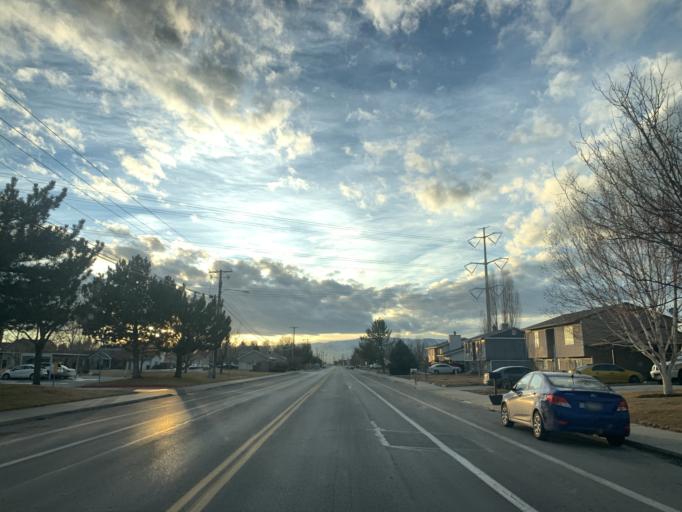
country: US
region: Utah
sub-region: Utah County
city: Provo
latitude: 40.2426
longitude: -111.6992
